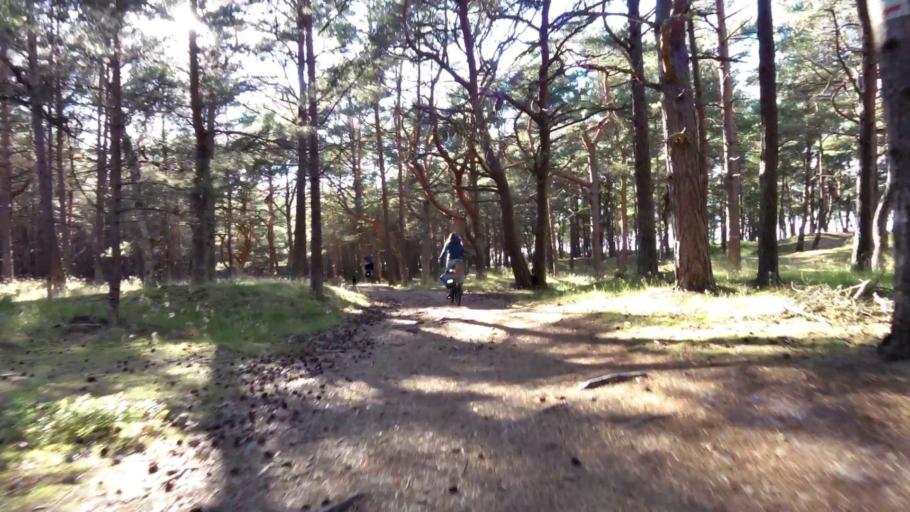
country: PL
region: West Pomeranian Voivodeship
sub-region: Powiat kolobrzeski
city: Grzybowo
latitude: 54.1645
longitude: 15.4429
